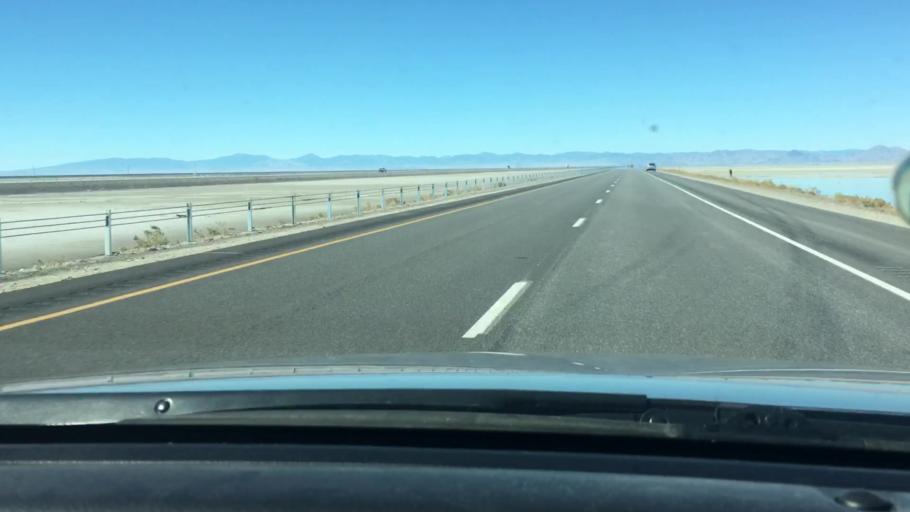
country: US
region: Utah
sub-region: Tooele County
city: Wendover
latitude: 40.7331
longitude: -113.5535
